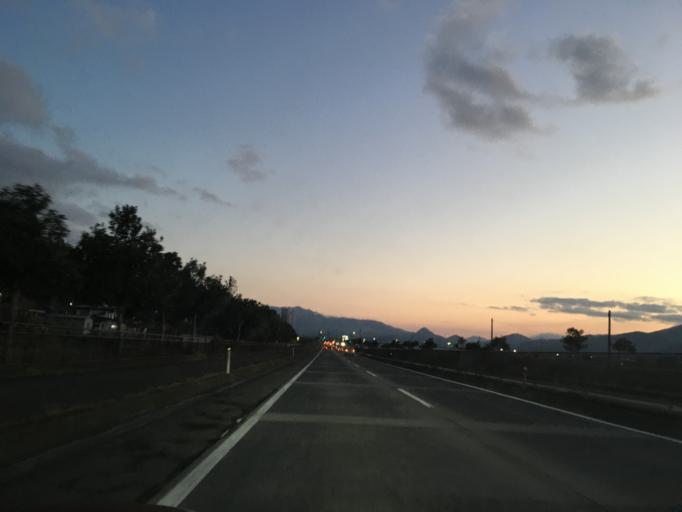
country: JP
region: Yamagata
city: Kaminoyama
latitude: 38.1574
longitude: 140.2979
